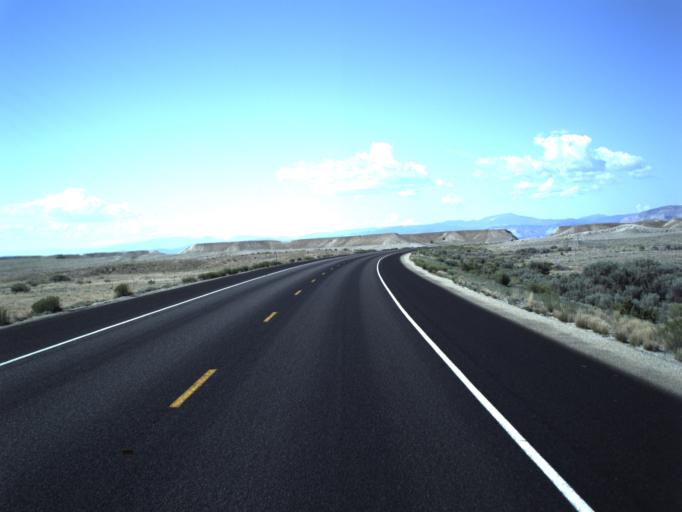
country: US
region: Utah
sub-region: Emery County
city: Ferron
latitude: 38.9747
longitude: -111.1779
